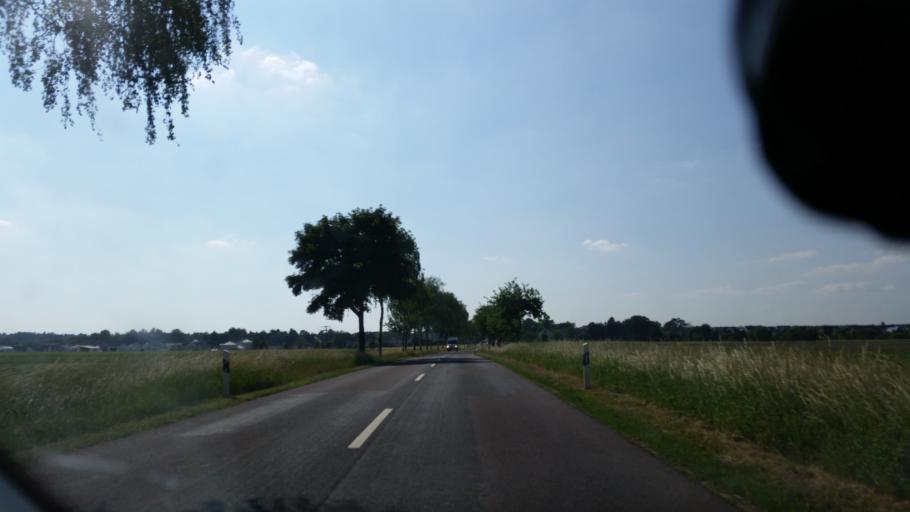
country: DE
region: Lower Saxony
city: Lehre
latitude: 52.3219
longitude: 10.6816
